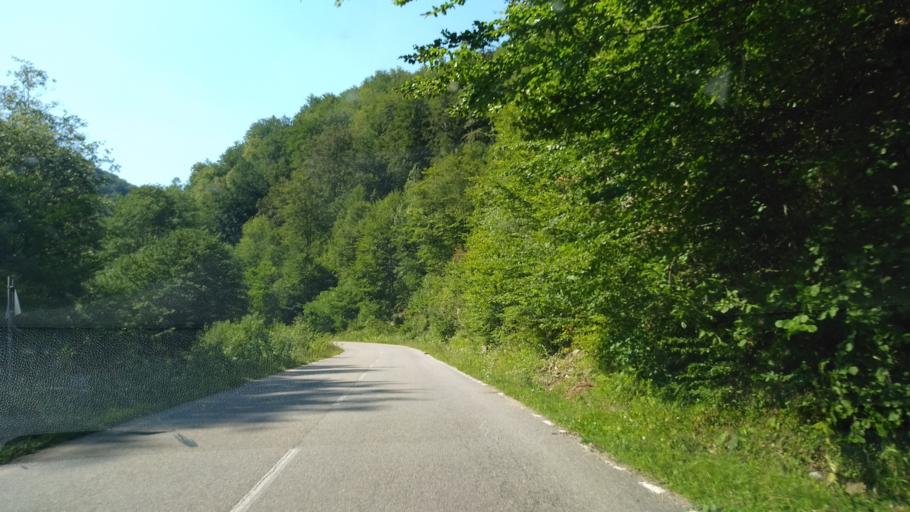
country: RO
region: Hunedoara
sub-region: Comuna Orastioara de Sus
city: Orastioara de Sus
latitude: 45.6346
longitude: 23.2022
